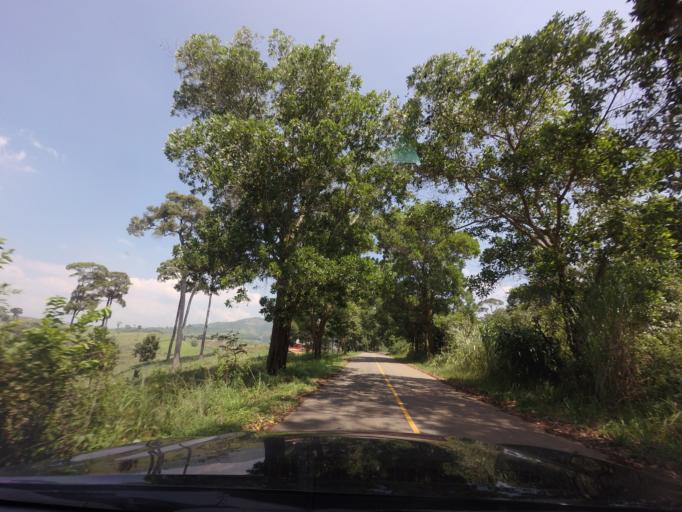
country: TH
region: Loei
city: Na Haeo
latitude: 17.5804
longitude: 100.9047
